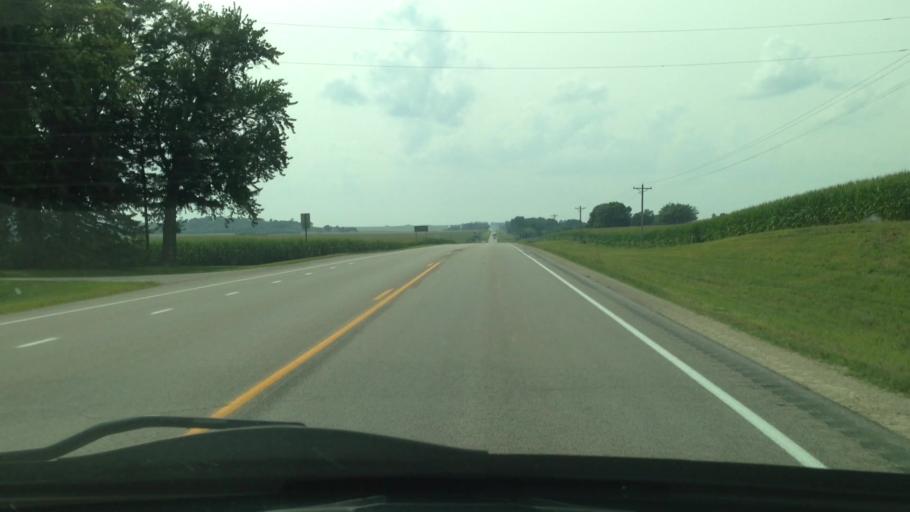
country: US
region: Minnesota
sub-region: Wabasha County
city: Elgin
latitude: 44.1654
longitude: -92.2609
